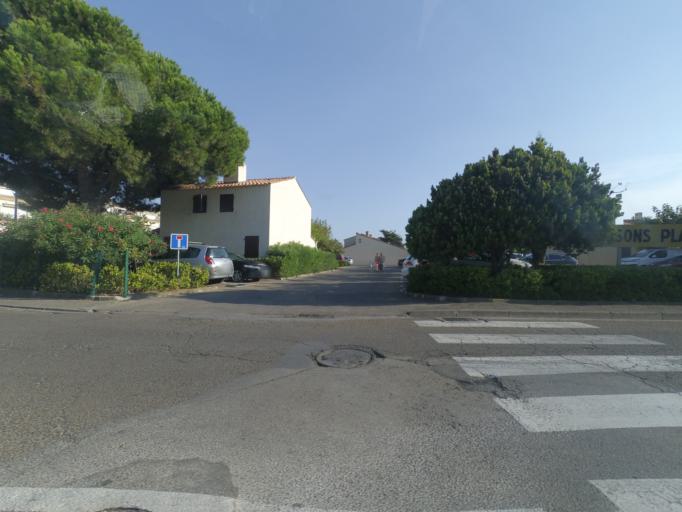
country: FR
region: Languedoc-Roussillon
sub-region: Departement du Gard
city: Le Grau-du-Roi
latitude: 43.5283
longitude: 4.1490
